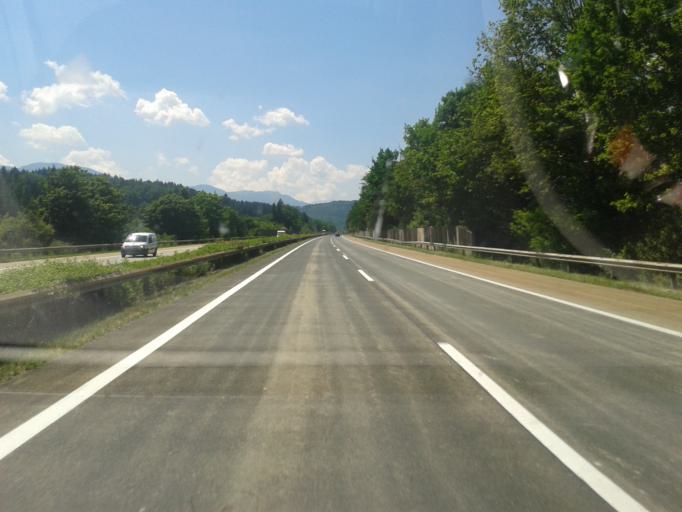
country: AT
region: Carinthia
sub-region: Villach Stadt
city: Villach
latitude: 46.5905
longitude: 13.8693
